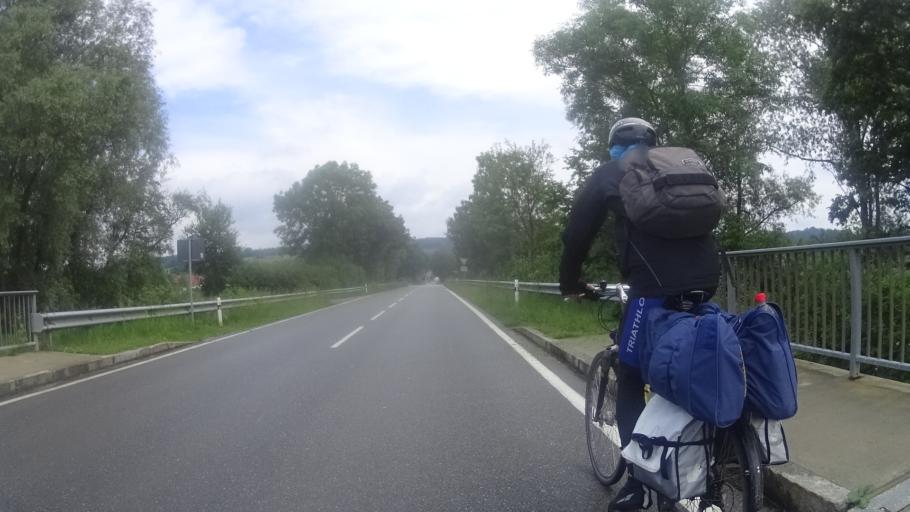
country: DE
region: Bavaria
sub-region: Lower Bavaria
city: Bad Birnbach
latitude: 48.4304
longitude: 13.1140
